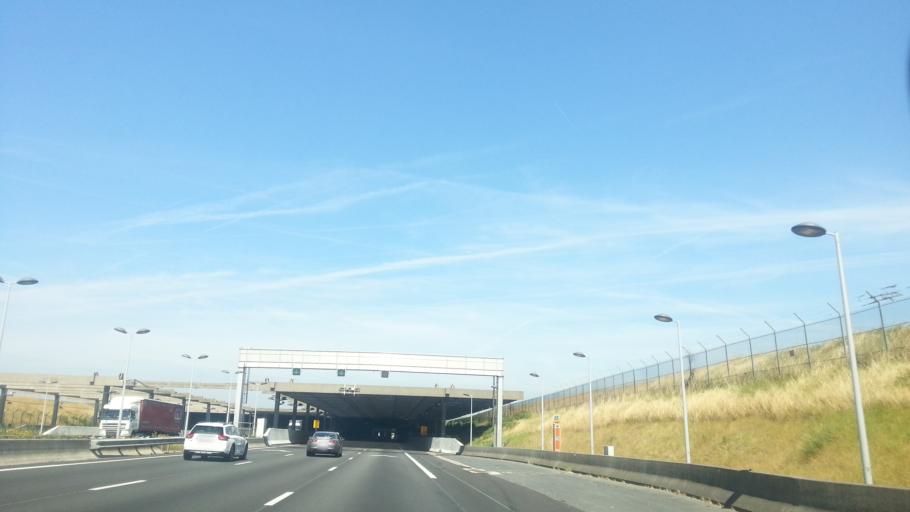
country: FR
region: Ile-de-France
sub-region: Departement du Val-d'Oise
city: Roissy-en-France
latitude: 49.0188
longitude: 2.5331
